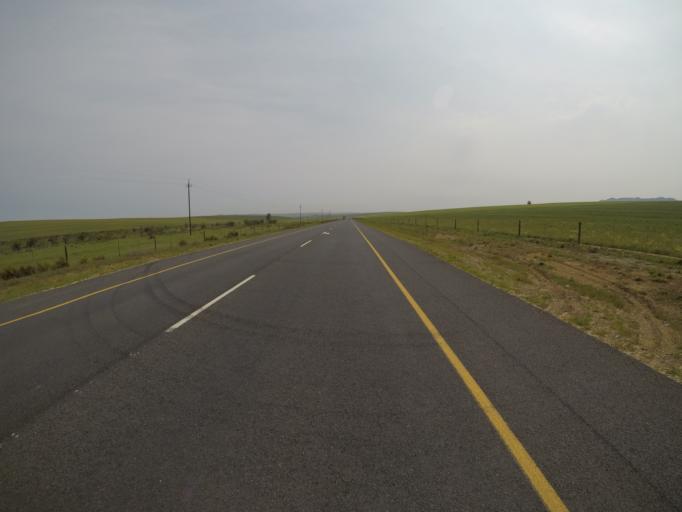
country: ZA
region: Western Cape
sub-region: West Coast District Municipality
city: Malmesbury
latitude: -33.4709
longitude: 18.7937
